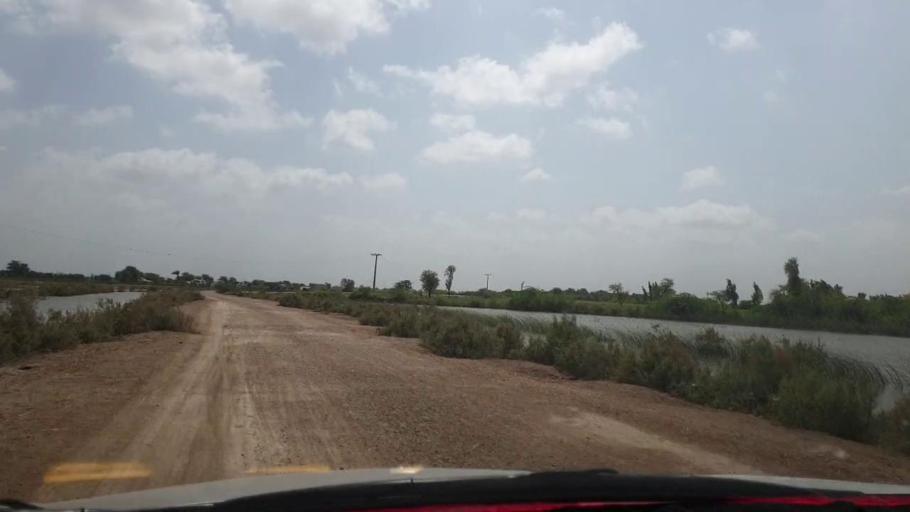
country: PK
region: Sindh
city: Talhar
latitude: 24.9039
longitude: 68.8585
